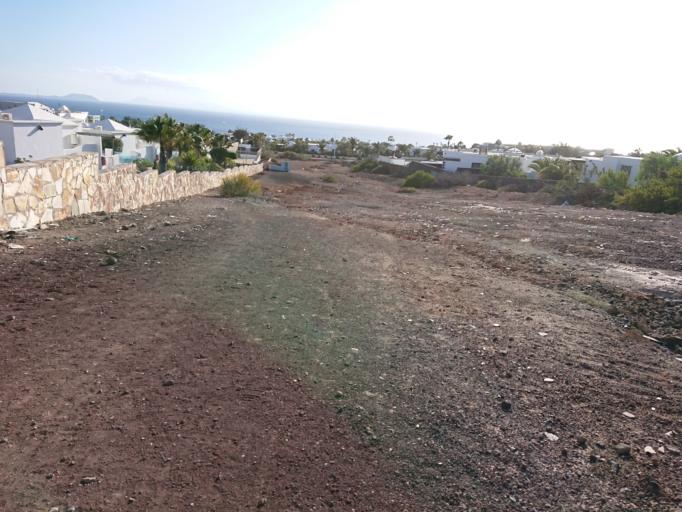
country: ES
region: Canary Islands
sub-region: Provincia de Las Palmas
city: Playa Blanca
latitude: 28.8671
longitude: -13.8477
